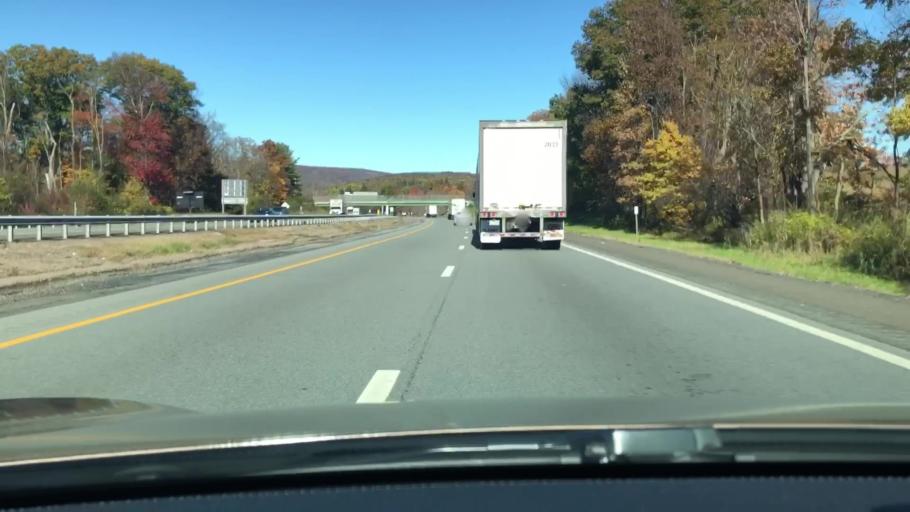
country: US
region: New York
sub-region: Orange County
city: Central Valley
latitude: 41.3232
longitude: -74.1126
